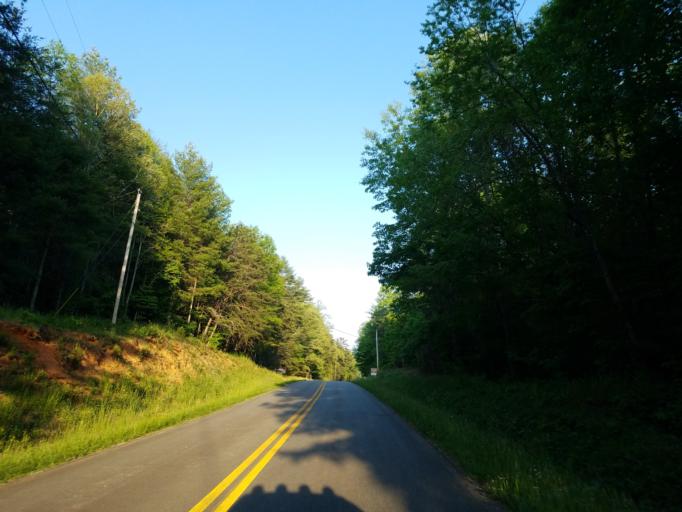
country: US
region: Georgia
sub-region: Union County
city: Blairsville
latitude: 34.7400
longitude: -84.0691
